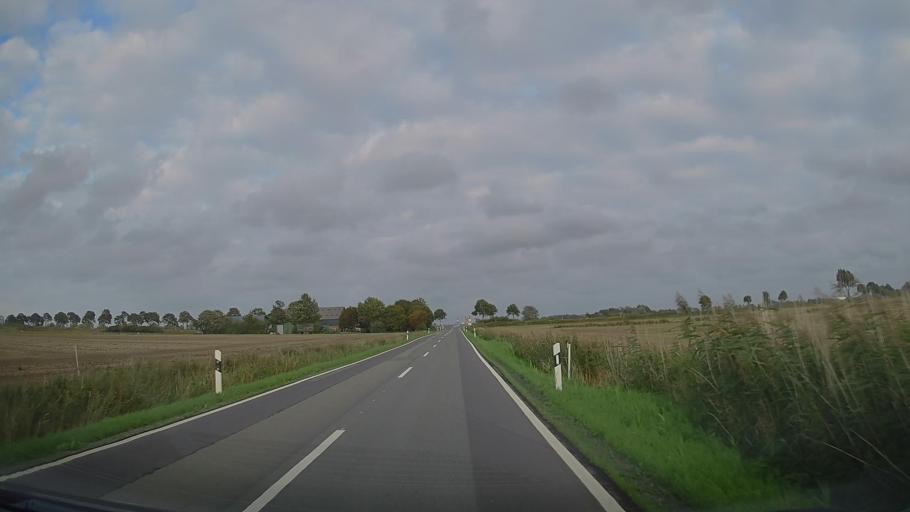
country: DE
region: Schleswig-Holstein
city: Husum
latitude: 54.4390
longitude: 9.0403
